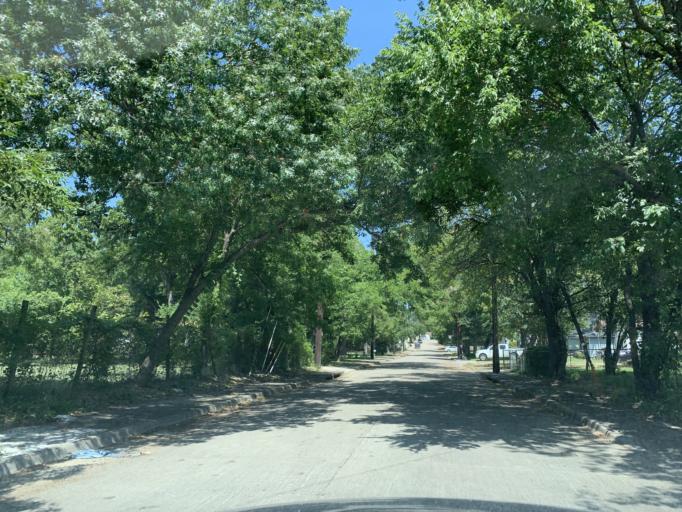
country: US
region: Texas
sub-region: Dallas County
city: Hutchins
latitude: 32.6832
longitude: -96.7912
